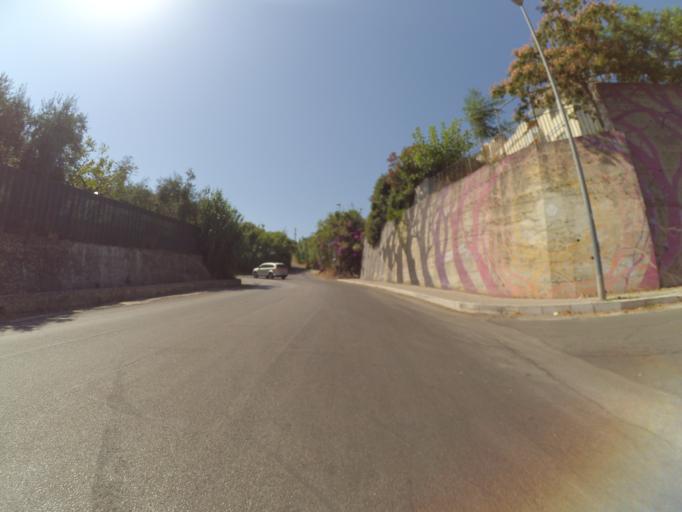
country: IT
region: Latium
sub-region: Provincia di Latina
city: Gaeta
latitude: 41.2170
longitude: 13.5595
